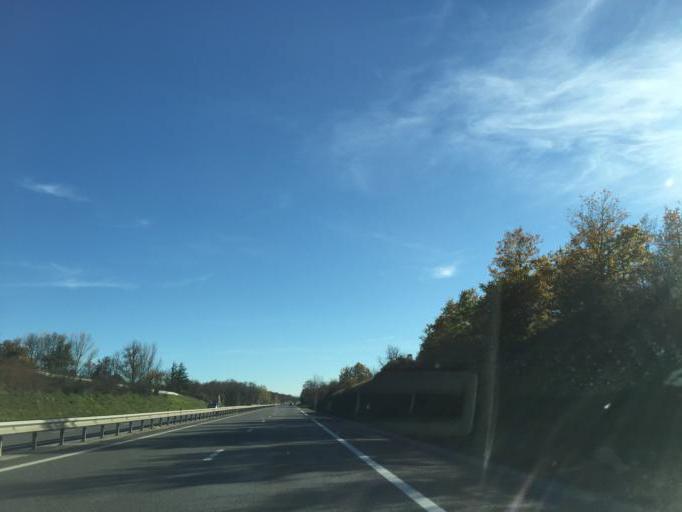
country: FR
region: Rhone-Alpes
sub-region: Departement de la Loire
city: Montrond-les-Bains
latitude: 45.6168
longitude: 4.2045
